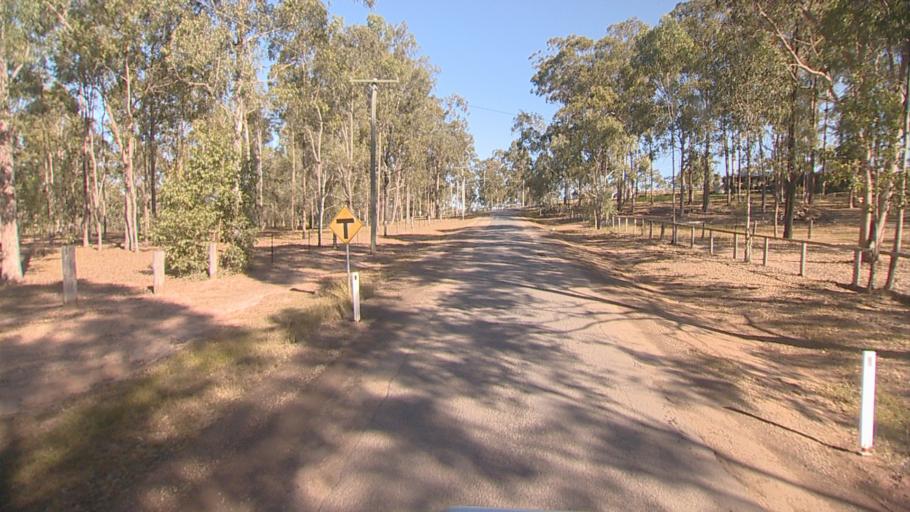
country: AU
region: Queensland
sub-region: Logan
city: Cedar Vale
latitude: -27.8539
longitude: 153.0156
